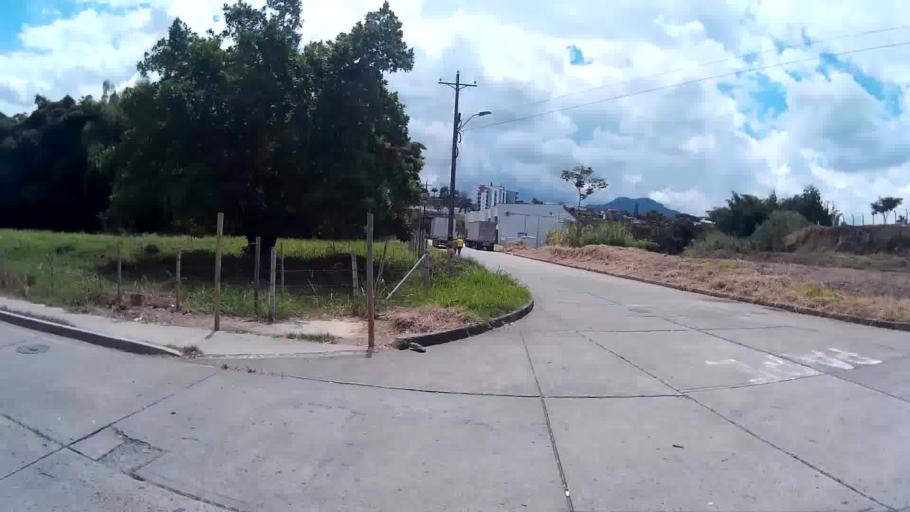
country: CO
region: Risaralda
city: Pereira
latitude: 4.8074
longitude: -75.7637
